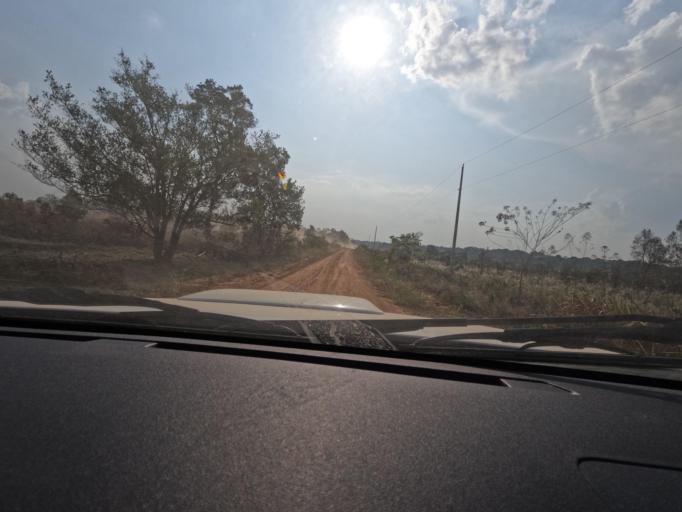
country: BR
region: Rondonia
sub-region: Porto Velho
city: Porto Velho
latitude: -8.5727
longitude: -64.0179
